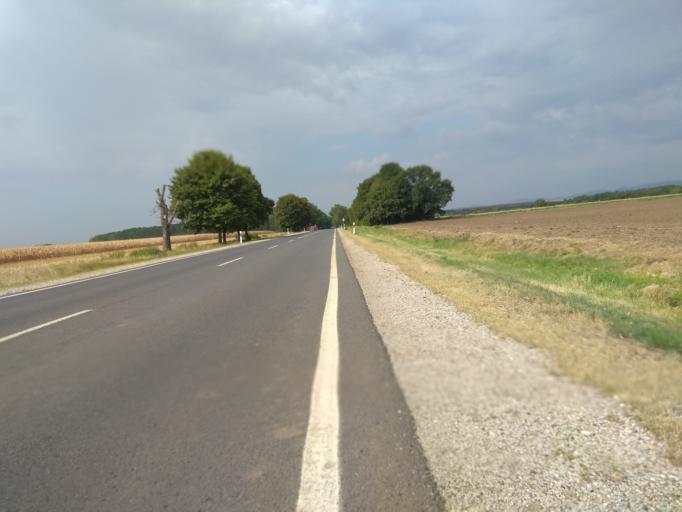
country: HU
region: Borsod-Abauj-Zemplen
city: Emod
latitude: 47.9285
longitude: 20.7903
